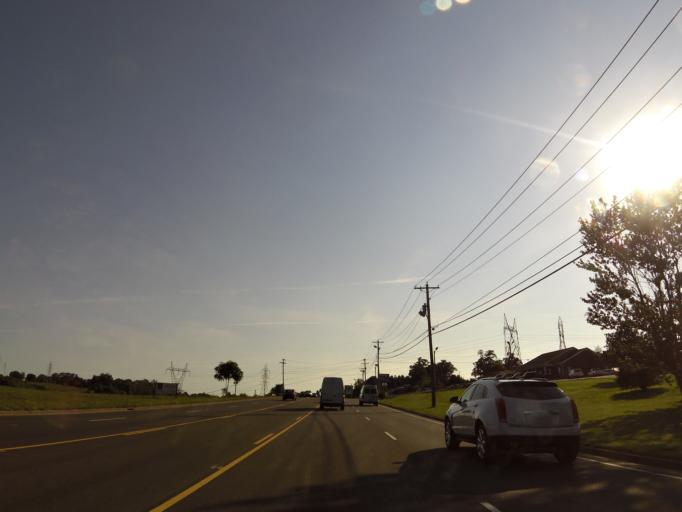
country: US
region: Tennessee
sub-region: Blount County
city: Maryville
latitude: 35.7221
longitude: -84.0051
